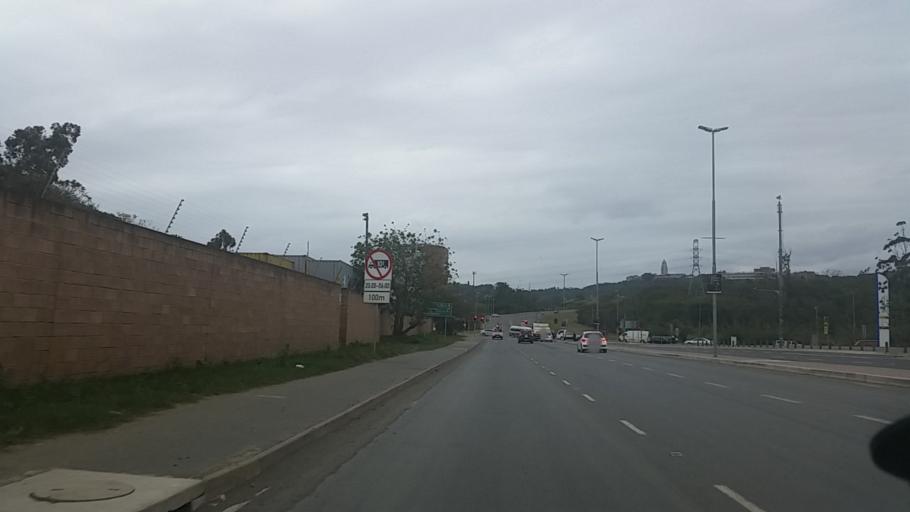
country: ZA
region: KwaZulu-Natal
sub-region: eThekwini Metropolitan Municipality
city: Berea
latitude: -29.8635
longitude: 30.9639
